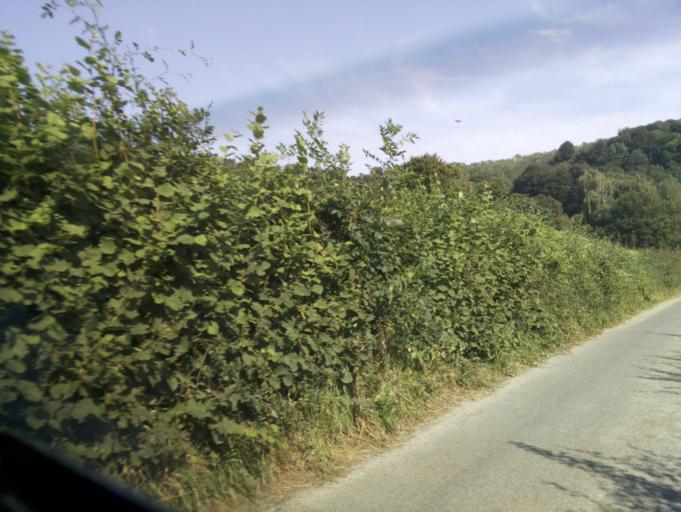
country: GB
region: England
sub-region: Gloucestershire
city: Dursley
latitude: 51.6921
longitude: -2.3185
